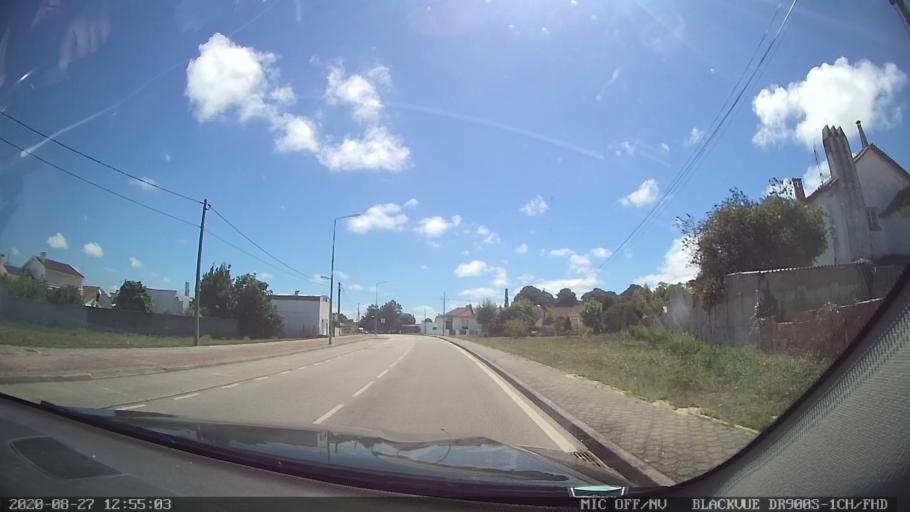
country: PT
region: Aveiro
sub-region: Ilhavo
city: Ilhavo
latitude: 40.5899
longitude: -8.6807
